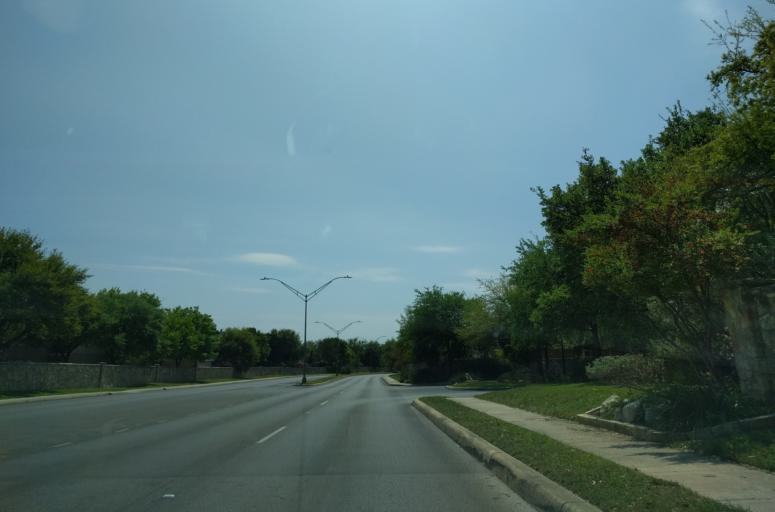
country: US
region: Texas
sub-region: Bexar County
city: Shavano Park
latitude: 29.5706
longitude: -98.5857
